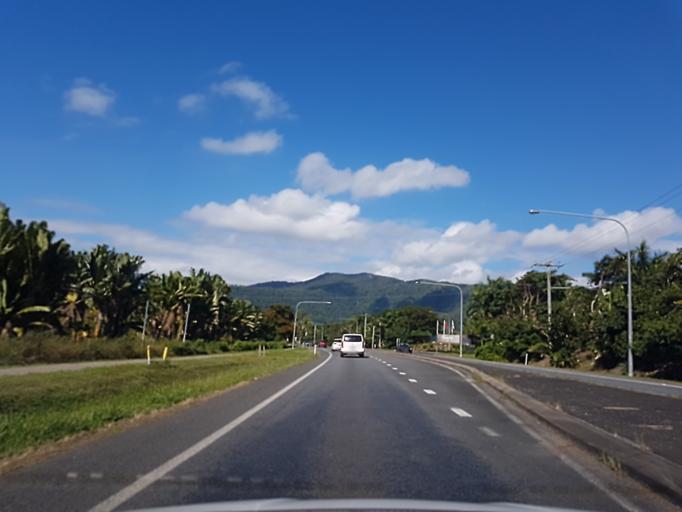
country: AU
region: Queensland
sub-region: Cairns
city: Trinity Beach
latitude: -16.7816
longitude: 145.6737
